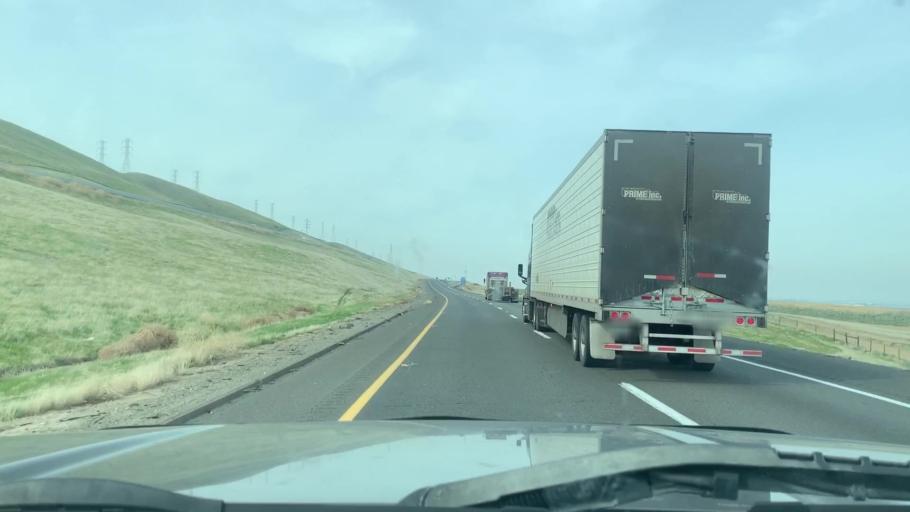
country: US
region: California
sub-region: Merced County
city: Los Banos
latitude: 36.9144
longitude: -120.8229
